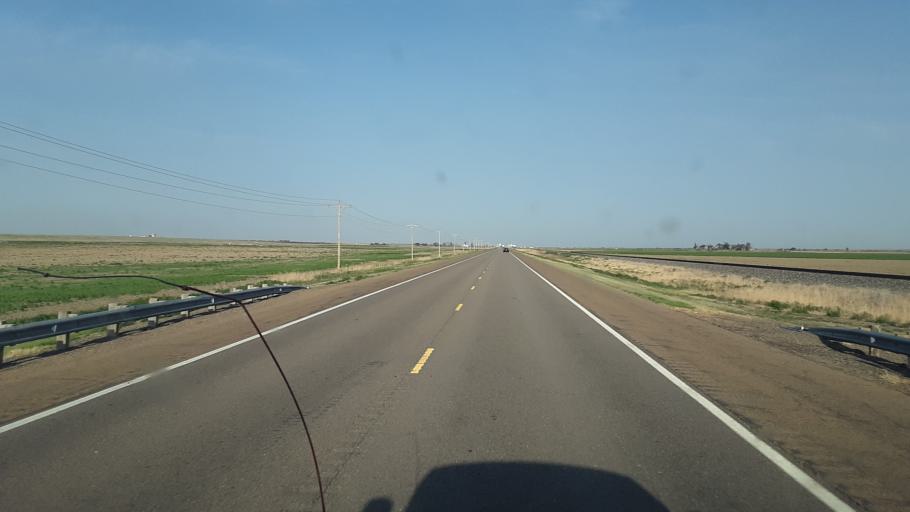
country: US
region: Kansas
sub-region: Hamilton County
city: Syracuse
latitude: 38.0043
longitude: -101.8450
